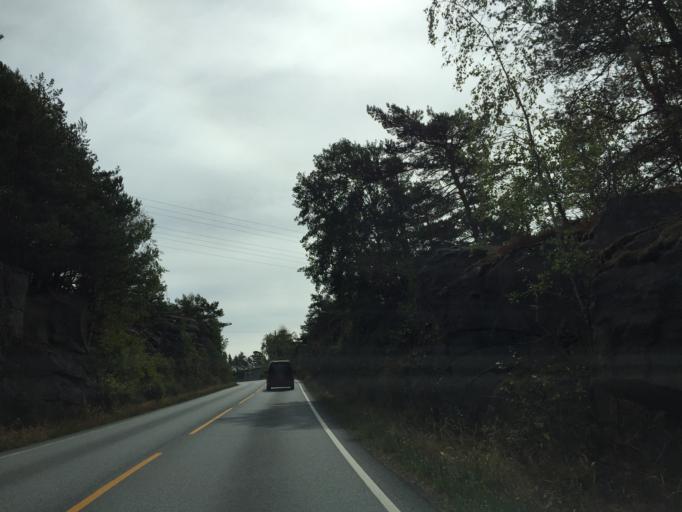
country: NO
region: Ostfold
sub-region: Fredrikstad
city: Fredrikstad
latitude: 59.0964
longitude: 10.9222
